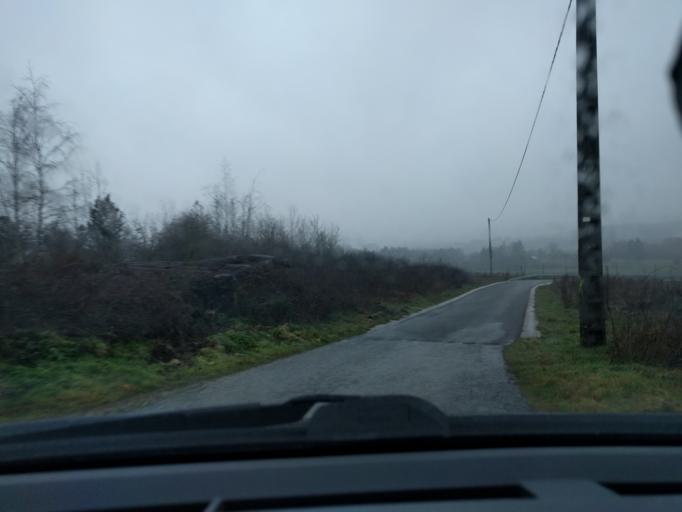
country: BE
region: Wallonia
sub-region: Province de Namur
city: Couvin
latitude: 50.0445
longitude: 4.5134
